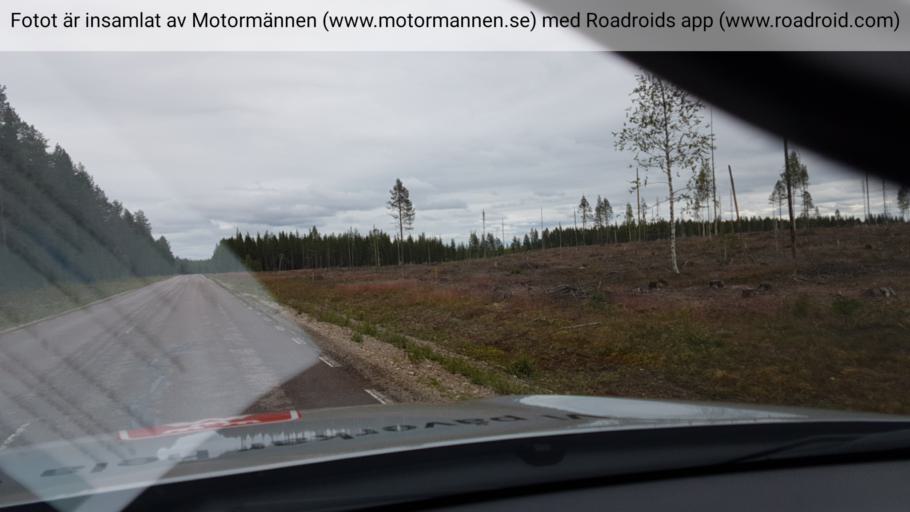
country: SE
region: Norrbotten
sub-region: Overkalix Kommun
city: OEverkalix
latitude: 67.0630
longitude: 22.2744
